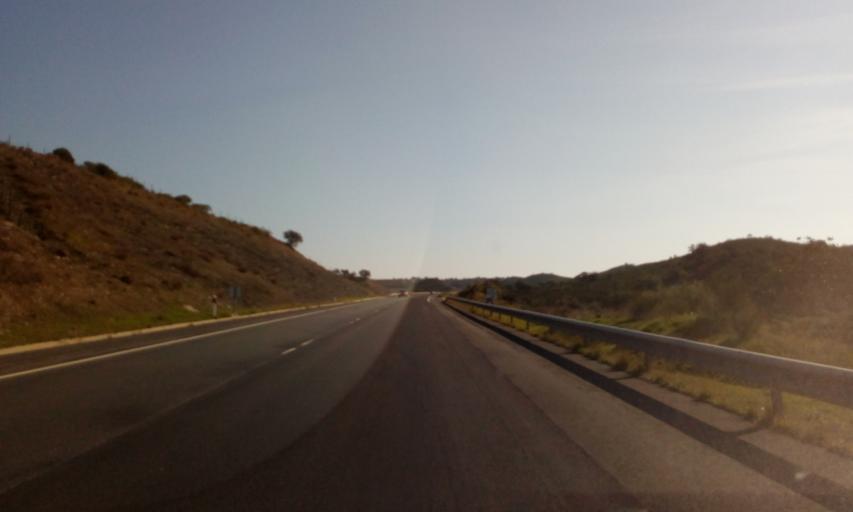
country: PT
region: Faro
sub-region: Castro Marim
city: Castro Marim
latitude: 37.2527
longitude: -7.4777
